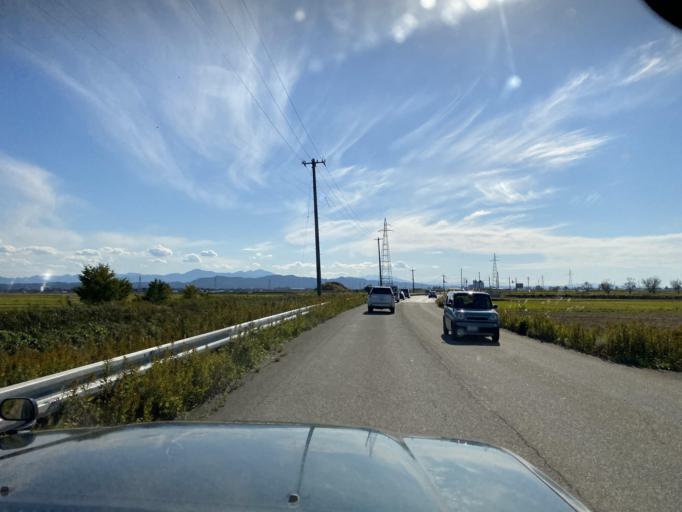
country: JP
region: Niigata
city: Niitsu-honcho
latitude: 37.8081
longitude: 139.0792
